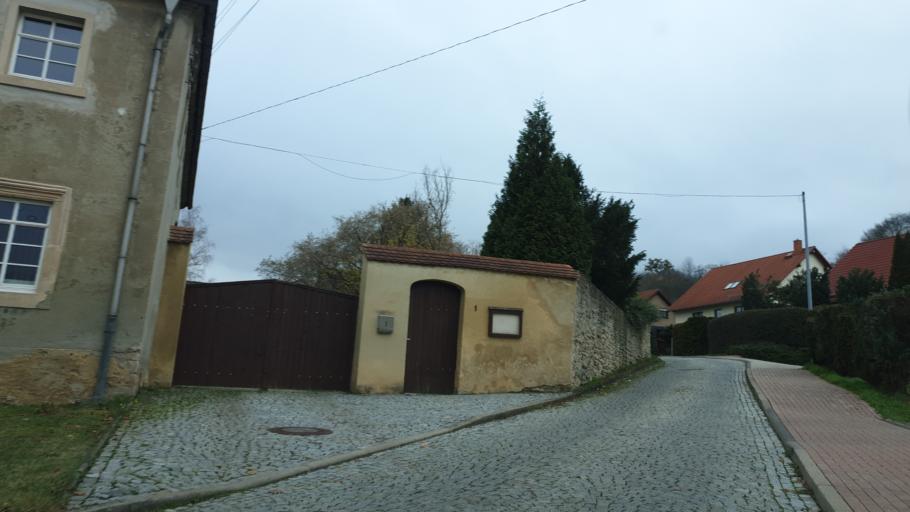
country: DE
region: Thuringia
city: Hartmannsdorf
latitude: 50.9759
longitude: 11.9743
